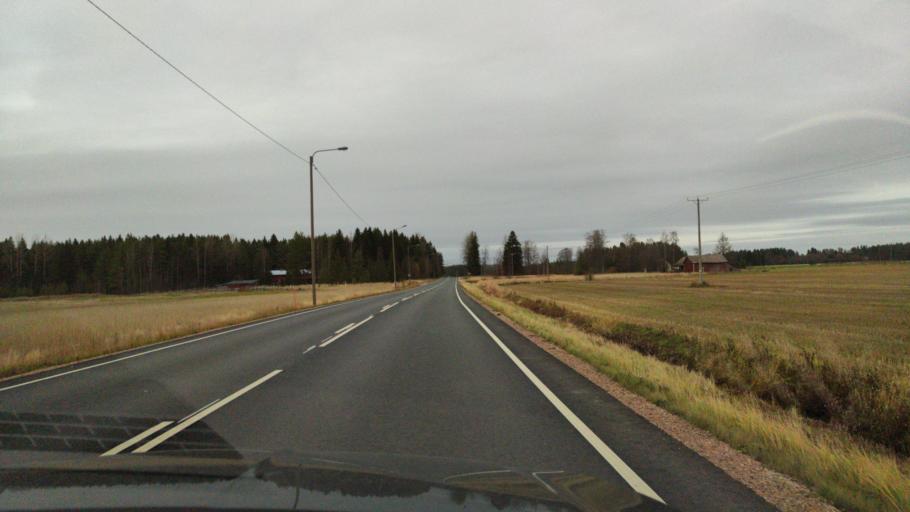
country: FI
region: Varsinais-Suomi
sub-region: Turku
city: Vahto
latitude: 60.6660
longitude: 22.4347
